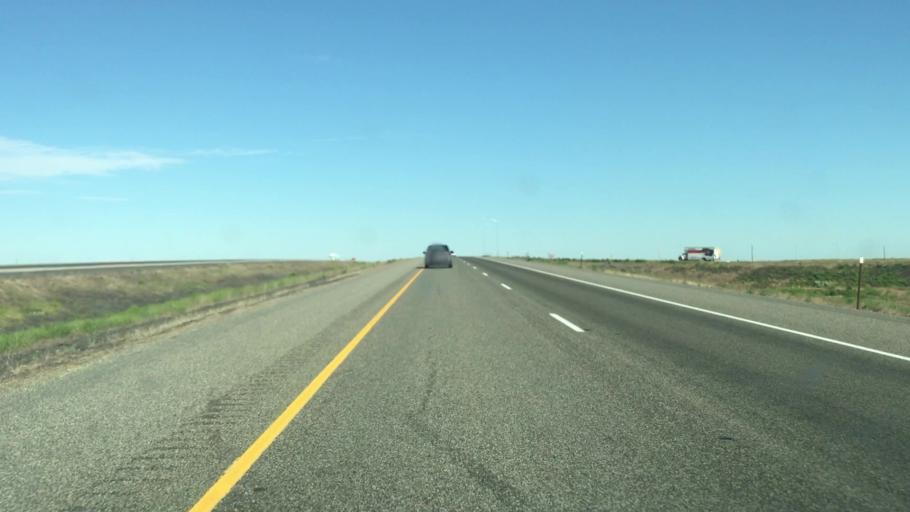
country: US
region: Idaho
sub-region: Twin Falls County
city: Twin Falls
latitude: 42.6404
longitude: -114.4399
